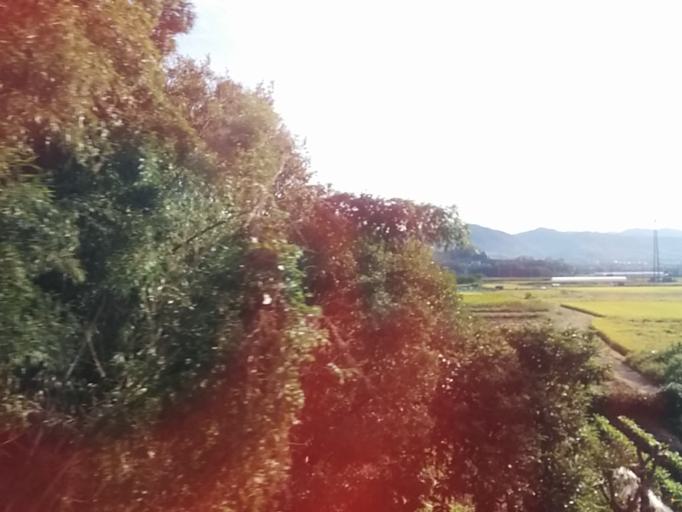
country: JP
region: Kyoto
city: Tanabe
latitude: 34.8050
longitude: 135.7814
